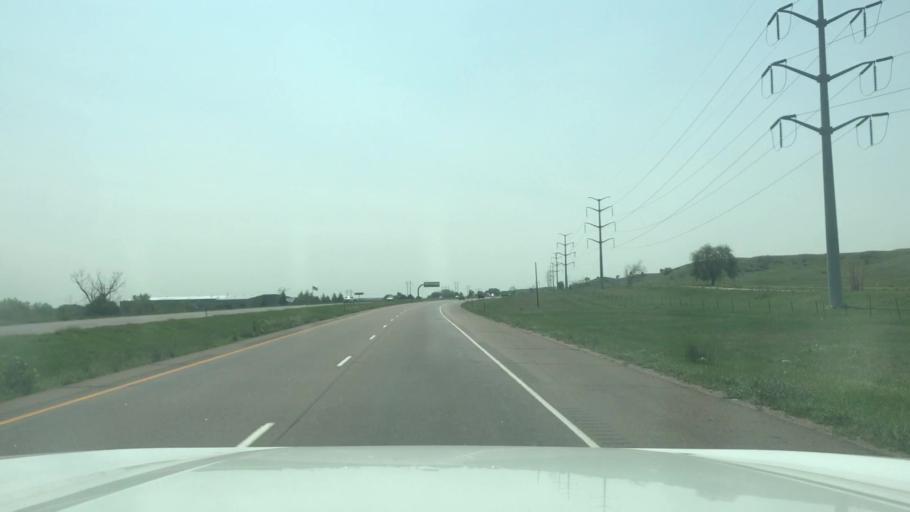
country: US
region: Colorado
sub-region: El Paso County
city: Fountain
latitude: 38.7080
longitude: -104.7240
